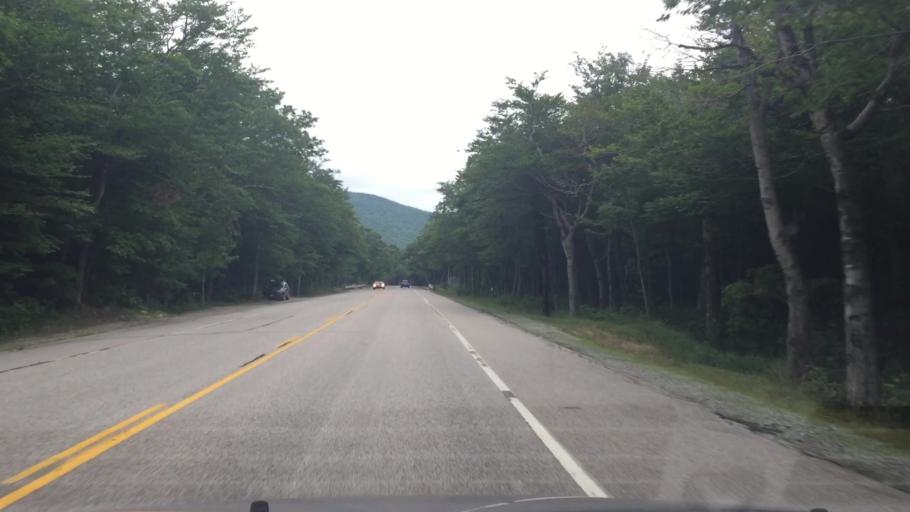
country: US
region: New Hampshire
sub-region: Carroll County
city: North Conway
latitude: 44.1592
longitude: -71.3653
